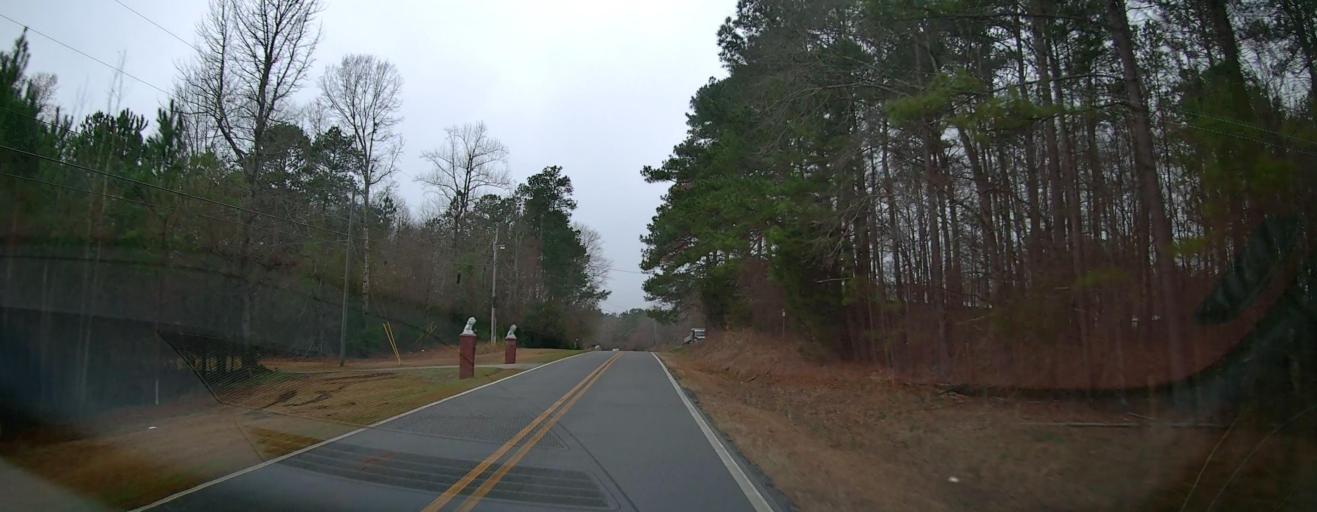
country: US
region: Georgia
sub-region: Monroe County
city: Forsyth
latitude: 33.1174
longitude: -83.9623
